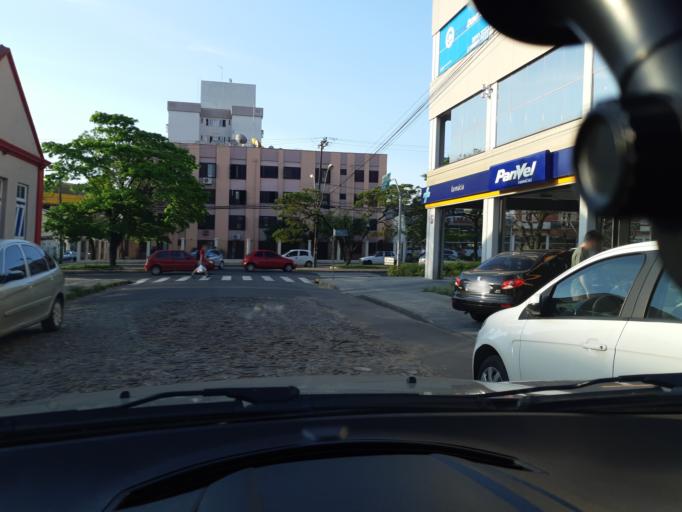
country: BR
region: Rio Grande do Sul
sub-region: Sao Leopoldo
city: Sao Leopoldo
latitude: -29.7704
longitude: -51.1405
